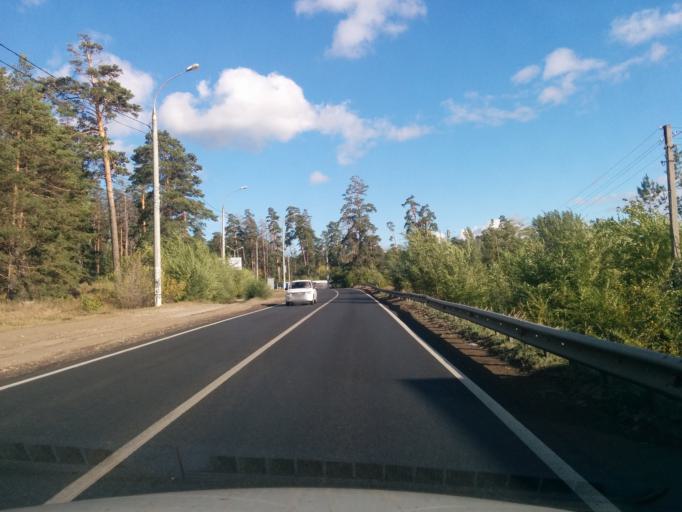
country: RU
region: Samara
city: Tol'yatti
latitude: 53.4769
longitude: 49.3246
